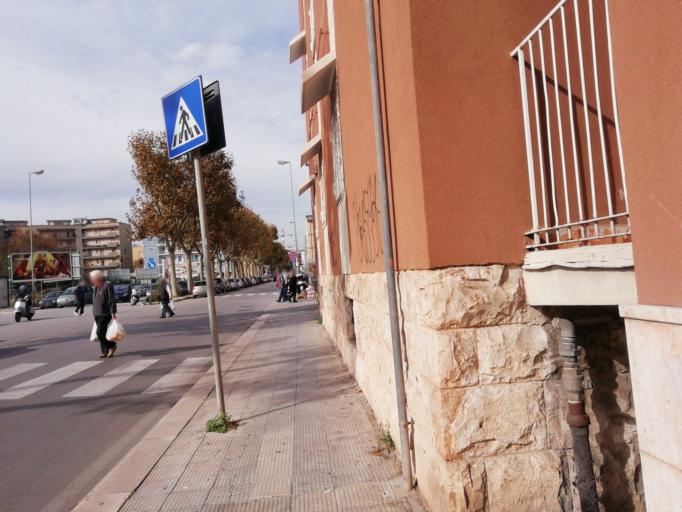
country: IT
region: Apulia
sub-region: Provincia di Bari
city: Bari
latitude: 41.1144
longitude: 16.8893
